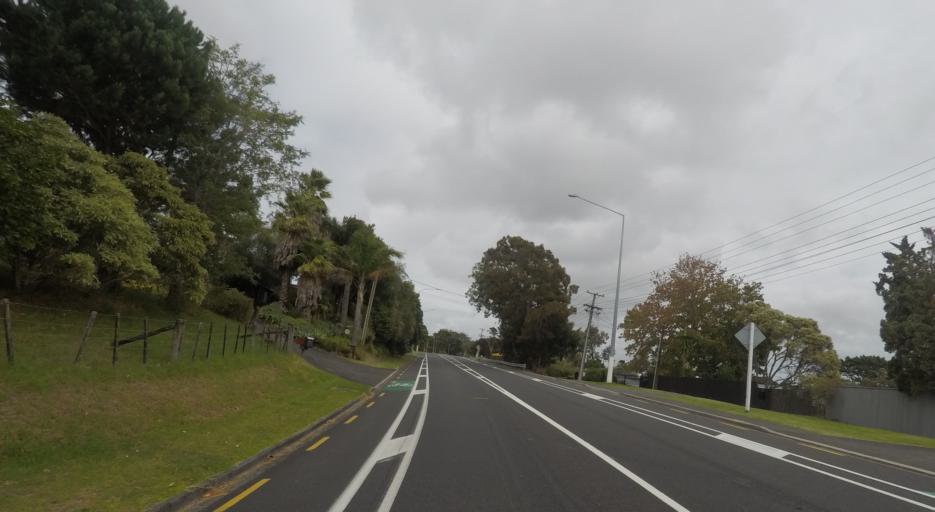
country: NZ
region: Auckland
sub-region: Auckland
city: North Shore
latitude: -36.7720
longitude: 174.6937
